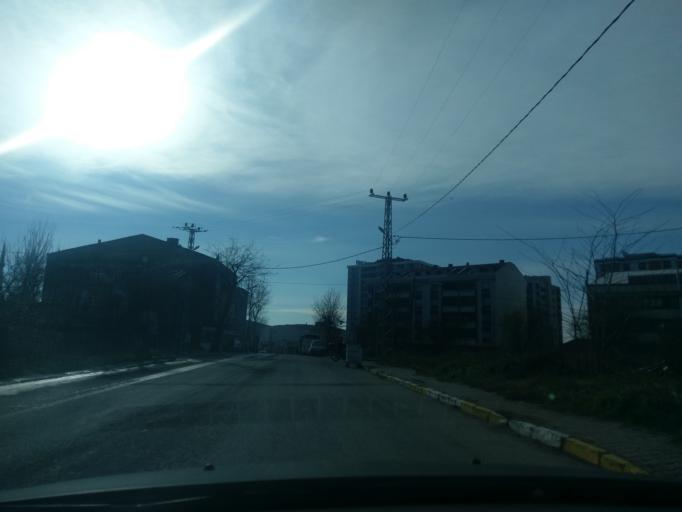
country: TR
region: Istanbul
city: Sultangazi
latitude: 41.1311
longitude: 28.8381
